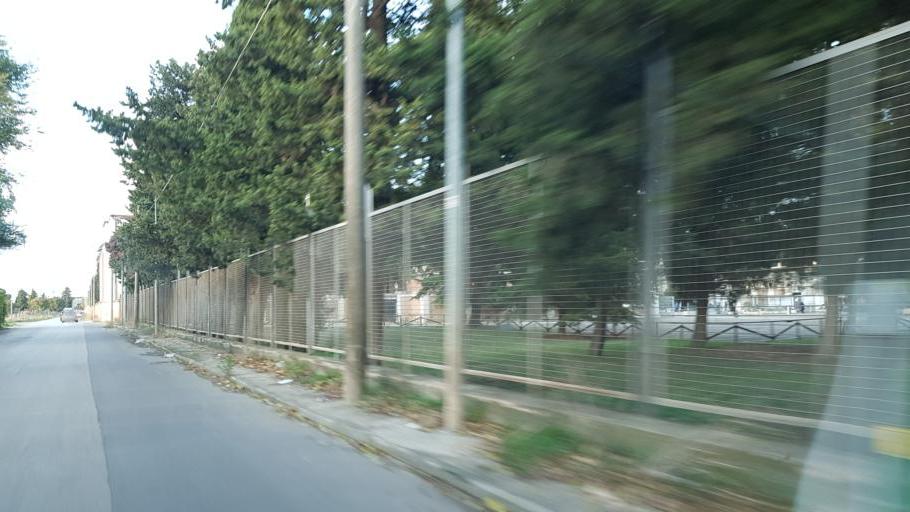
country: IT
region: Apulia
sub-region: Provincia di Foggia
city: Foggia
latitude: 41.4723
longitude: 15.5479
